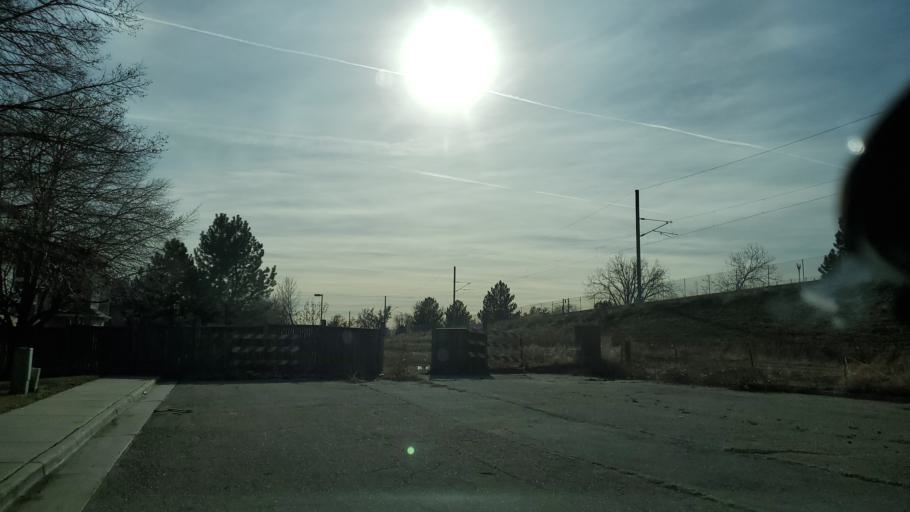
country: US
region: Colorado
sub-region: Adams County
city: Northglenn
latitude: 39.9132
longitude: -104.9579
